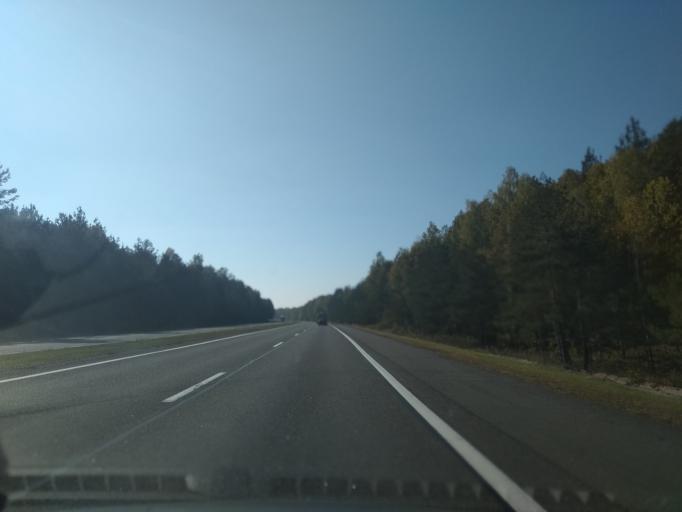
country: BY
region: Brest
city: Ivatsevichy
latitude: 52.8298
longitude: 25.5986
